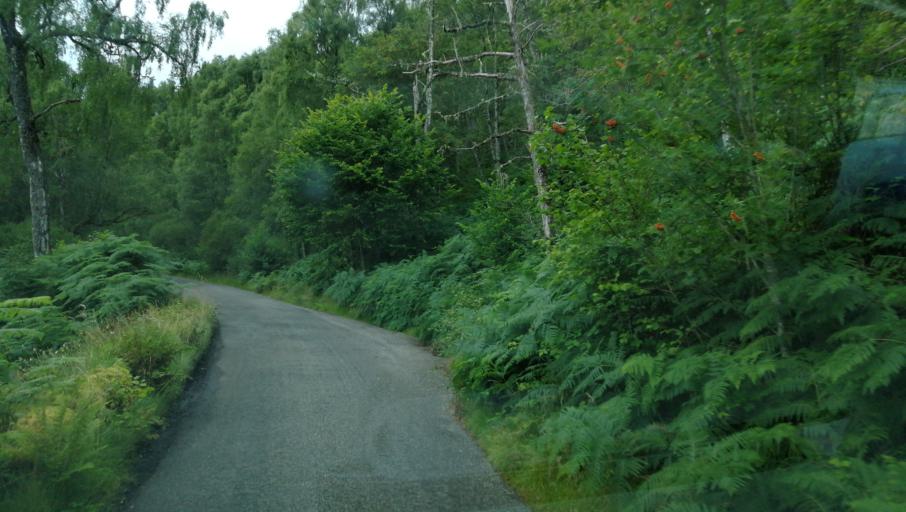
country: GB
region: Scotland
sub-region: Highland
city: Beauly
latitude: 57.3142
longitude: -4.8408
